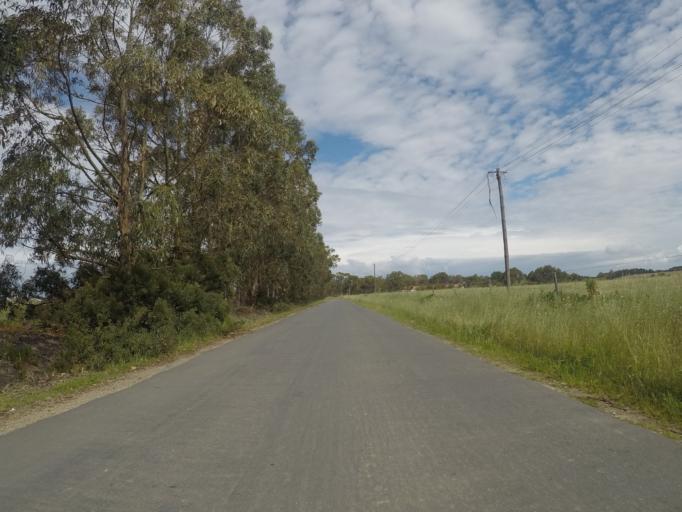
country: PT
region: Beja
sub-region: Odemira
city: Sao Teotonio
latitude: 37.4933
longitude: -8.7837
